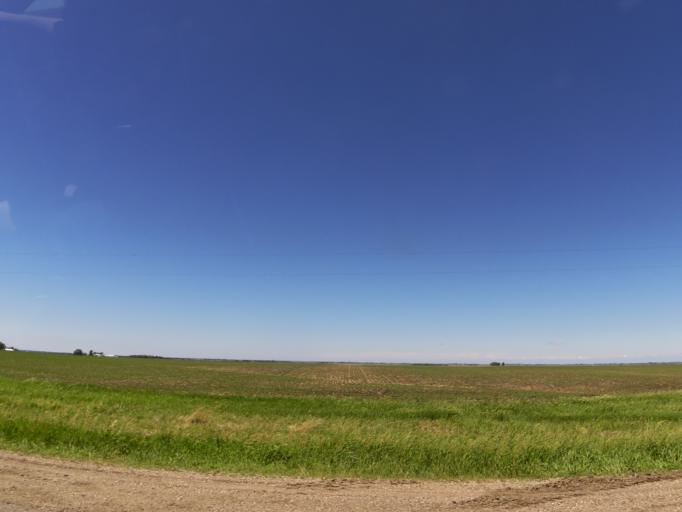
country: US
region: Minnesota
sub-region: Becker County
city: Detroit Lakes
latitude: 47.0154
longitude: -95.9124
